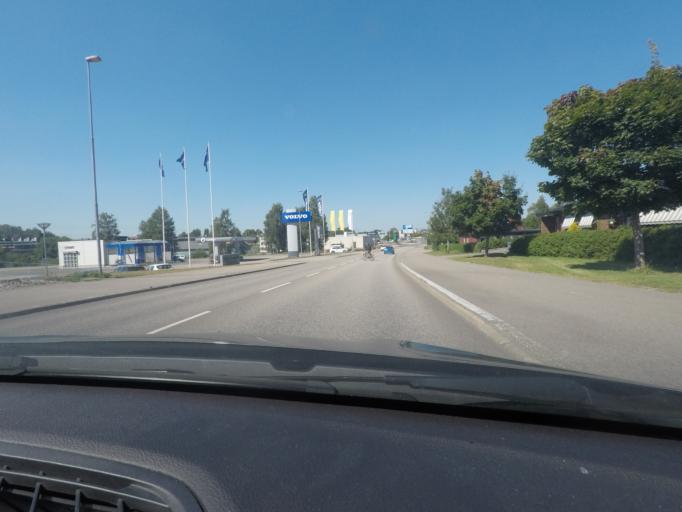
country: SE
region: Kronoberg
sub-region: Markaryds Kommun
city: Markaryd
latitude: 56.4549
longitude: 13.5947
